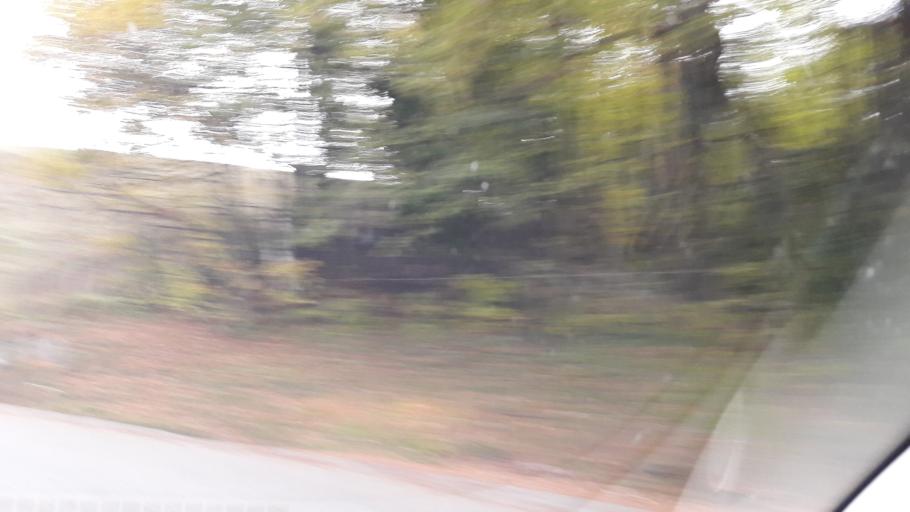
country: FR
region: Rhone-Alpes
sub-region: Departement de la Savoie
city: Saint-Jean-de-Maurienne
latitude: 45.2780
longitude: 6.3357
